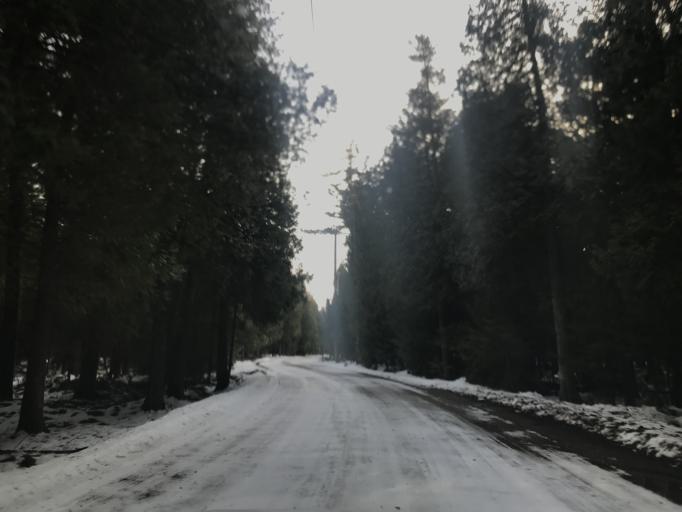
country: US
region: Wisconsin
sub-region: Door County
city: Sturgeon Bay
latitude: 45.1406
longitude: -87.0486
